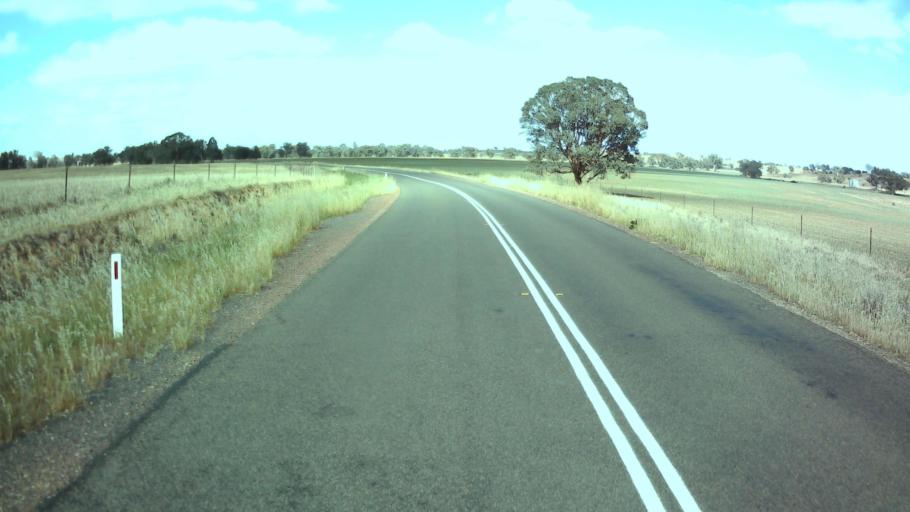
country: AU
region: New South Wales
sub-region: Weddin
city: Grenfell
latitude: -33.9781
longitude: 148.4217
